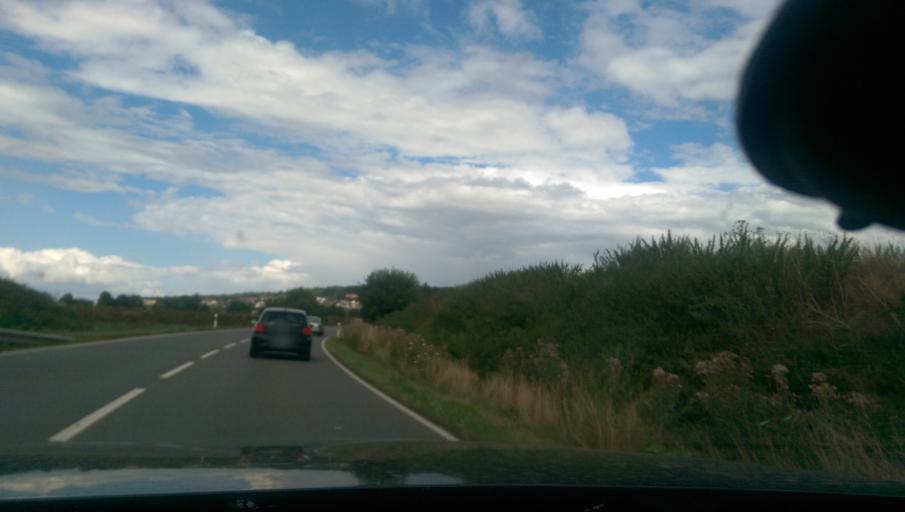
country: DE
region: Lower Saxony
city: Northeim
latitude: 51.7094
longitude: 9.9782
